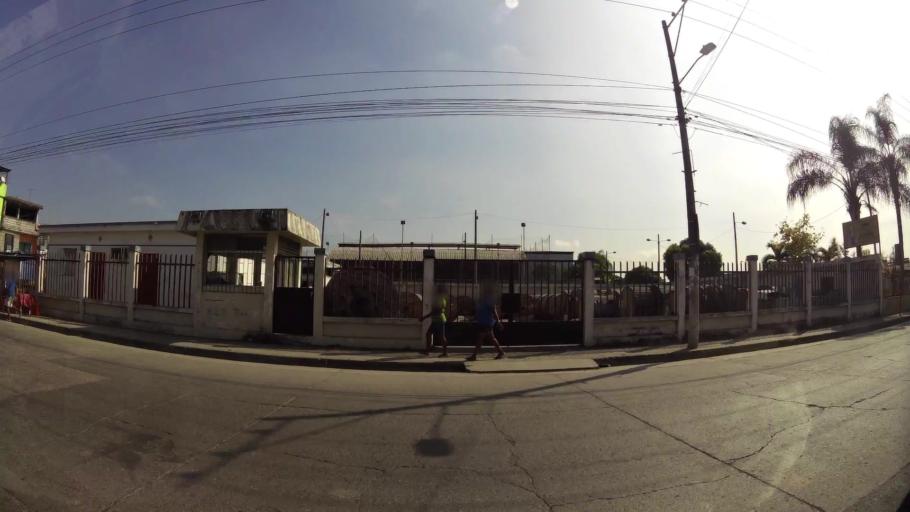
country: EC
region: Guayas
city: Eloy Alfaro
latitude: -2.1689
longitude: -79.8021
